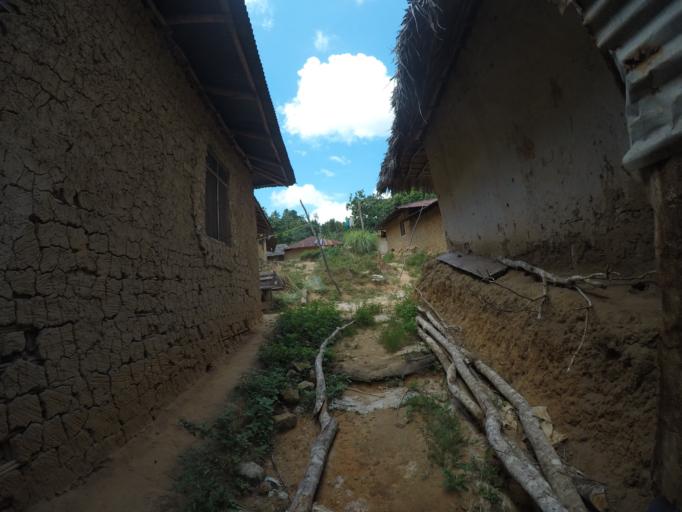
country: TZ
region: Pemba South
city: Mtambile
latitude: -5.3810
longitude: 39.7138
